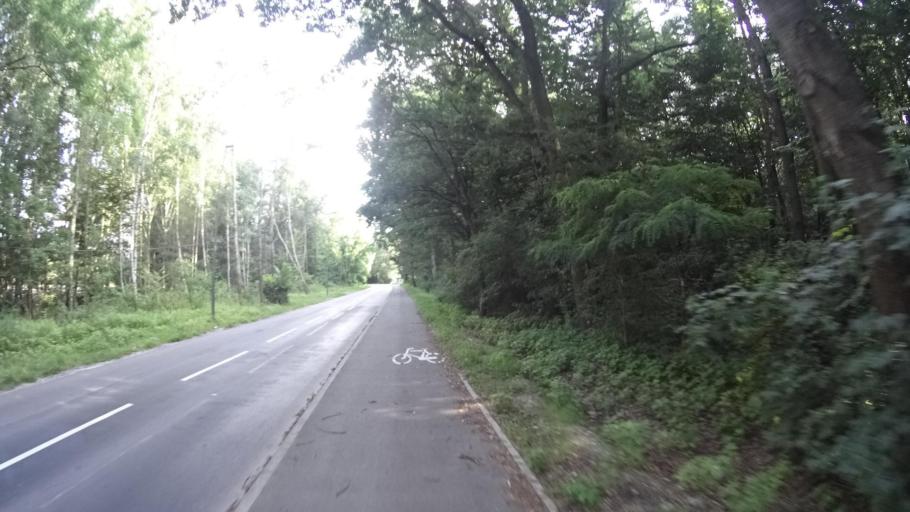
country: PL
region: Masovian Voivodeship
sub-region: Powiat pruszkowski
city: Nadarzyn
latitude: 52.0320
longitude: 20.7826
